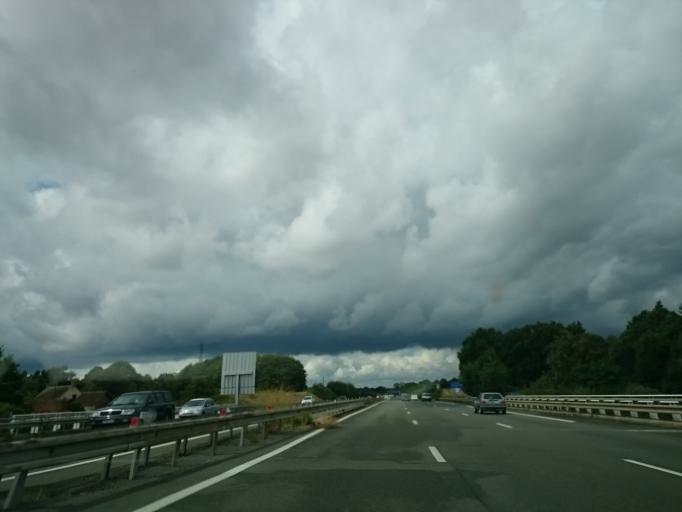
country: FR
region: Pays de la Loire
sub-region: Departement de la Sarthe
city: Sarge-les-le-Mans
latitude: 48.0517
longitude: 0.2651
